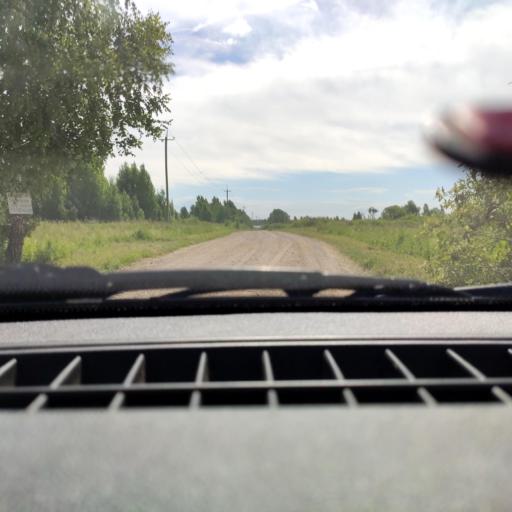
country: RU
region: Bashkortostan
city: Kabakovo
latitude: 54.7298
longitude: 56.2014
